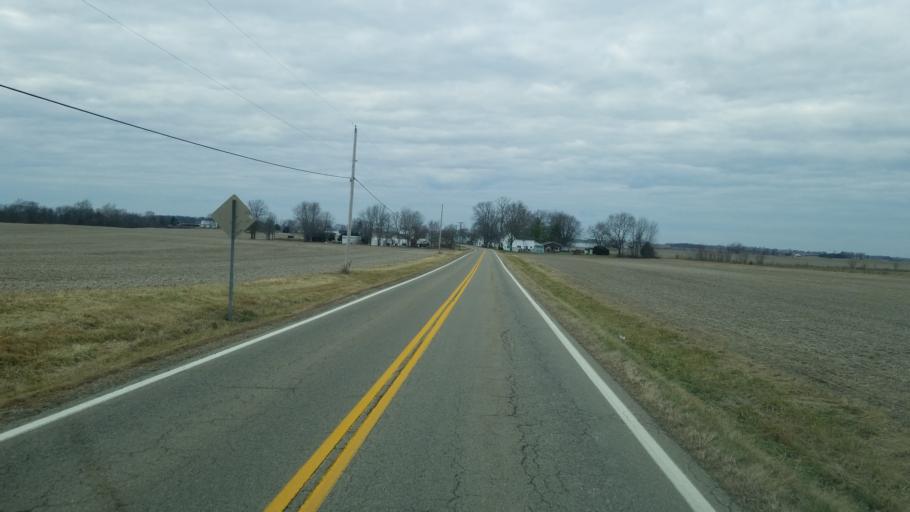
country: US
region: Ohio
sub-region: Highland County
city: Greenfield
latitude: 39.3537
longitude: -83.2994
